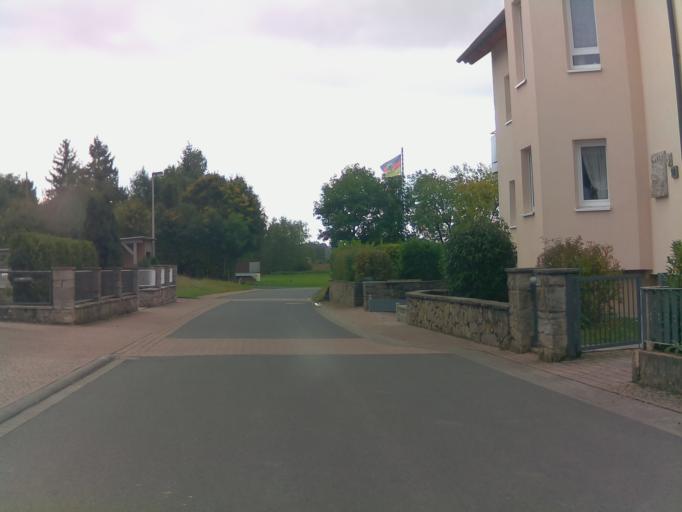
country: DE
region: Bavaria
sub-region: Regierungsbezirk Unterfranken
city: Kleinrinderfeld
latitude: 49.6969
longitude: 9.8419
